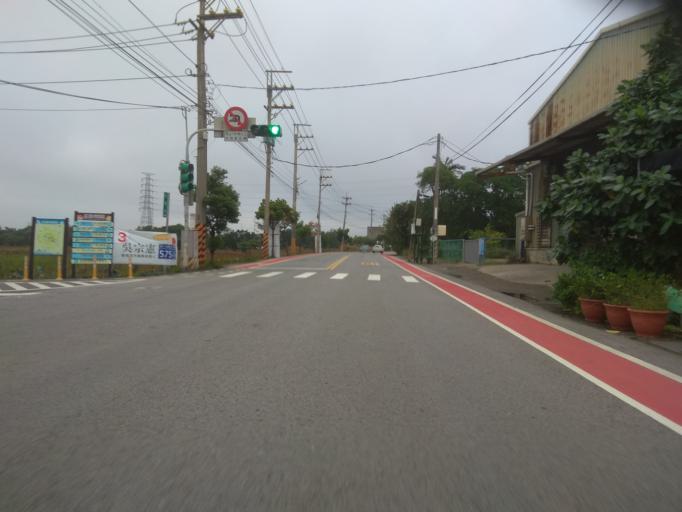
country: TW
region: Taiwan
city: Taoyuan City
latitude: 24.9996
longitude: 121.1220
